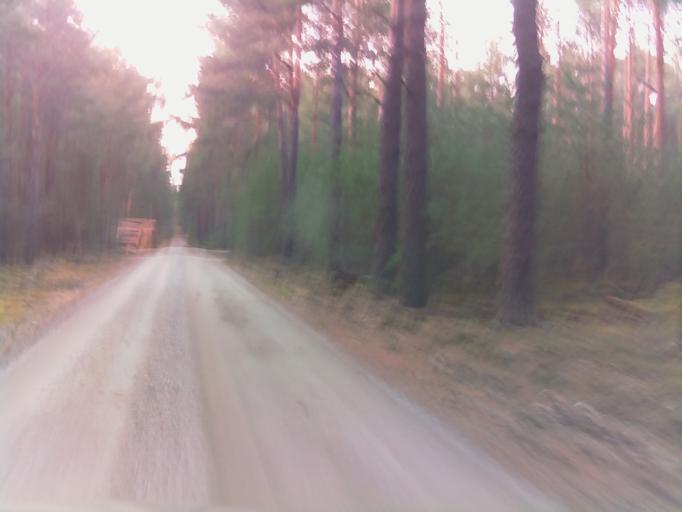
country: DE
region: Brandenburg
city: Tauer
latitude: 51.9698
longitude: 14.4458
